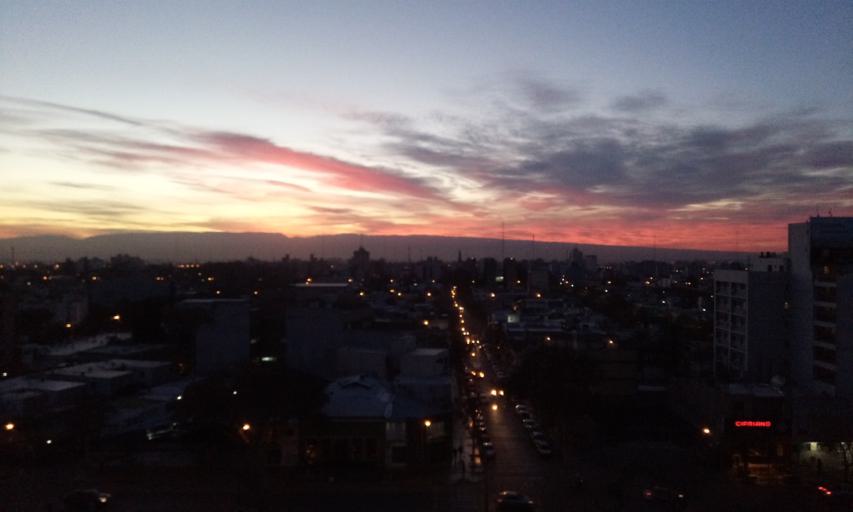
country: AR
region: San Juan
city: San Juan
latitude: -31.5374
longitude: -68.5374
